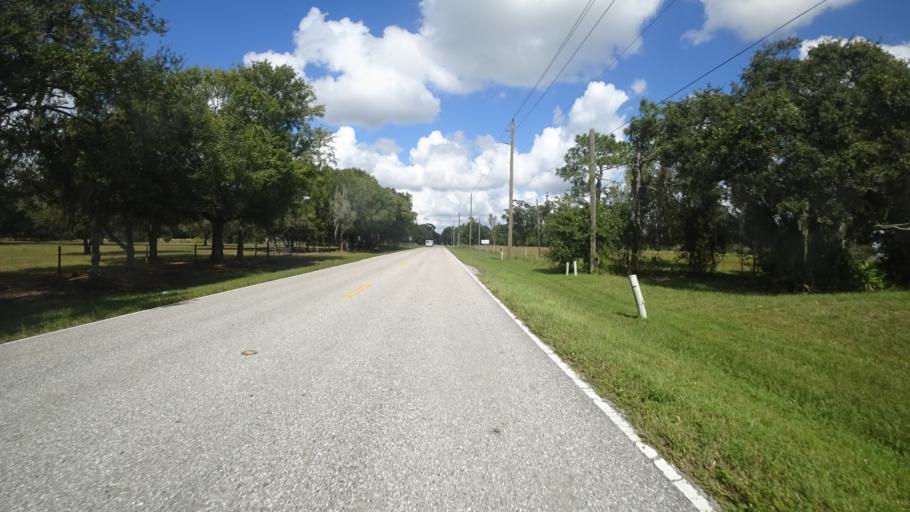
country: US
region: Florida
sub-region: Sarasota County
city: Lake Sarasota
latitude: 27.3843
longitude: -82.2682
